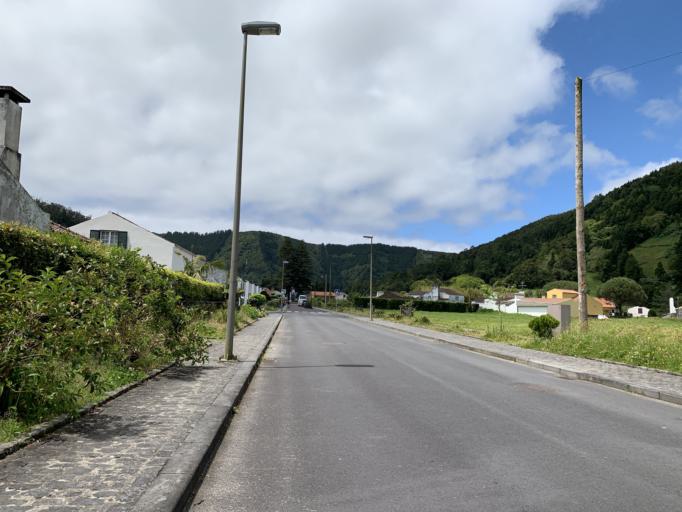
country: PT
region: Azores
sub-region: Ponta Delgada
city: Arrifes
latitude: 37.8636
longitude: -25.7931
